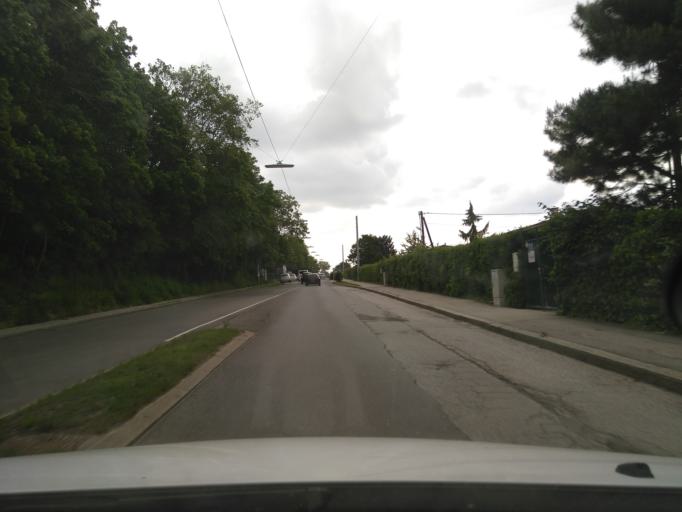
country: AT
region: Lower Austria
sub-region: Politischer Bezirk Modling
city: Perchtoldsdorf
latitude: 48.1585
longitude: 16.2912
